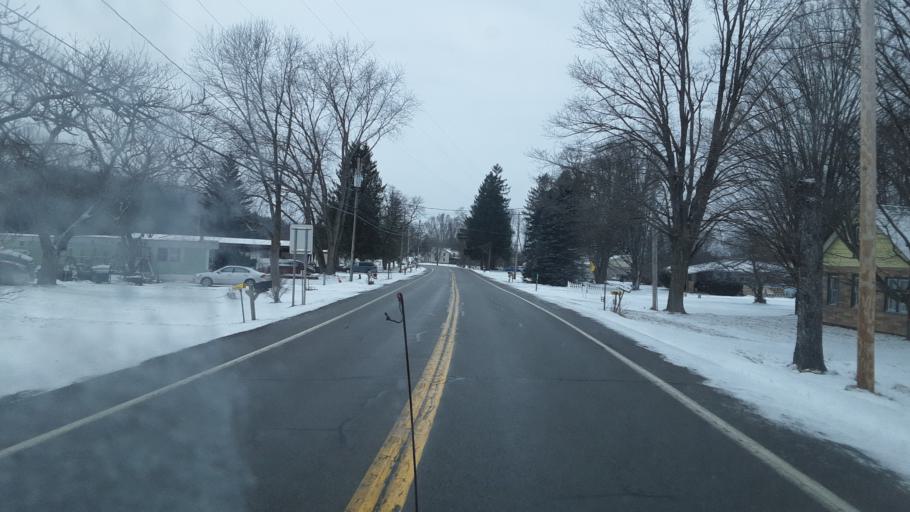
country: US
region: New York
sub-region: Allegany County
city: Wellsville
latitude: 42.1515
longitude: -77.9749
